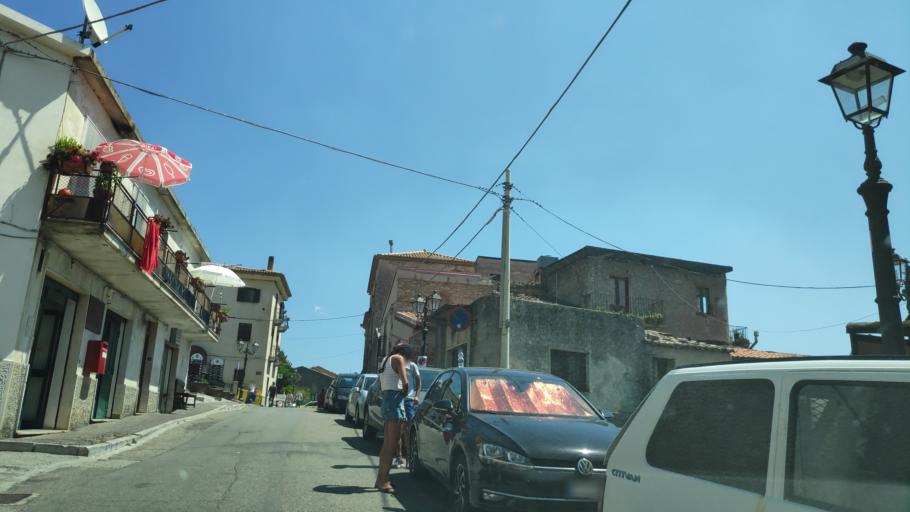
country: IT
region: Calabria
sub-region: Provincia di Reggio Calabria
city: Bova
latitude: 37.9942
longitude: 15.9321
